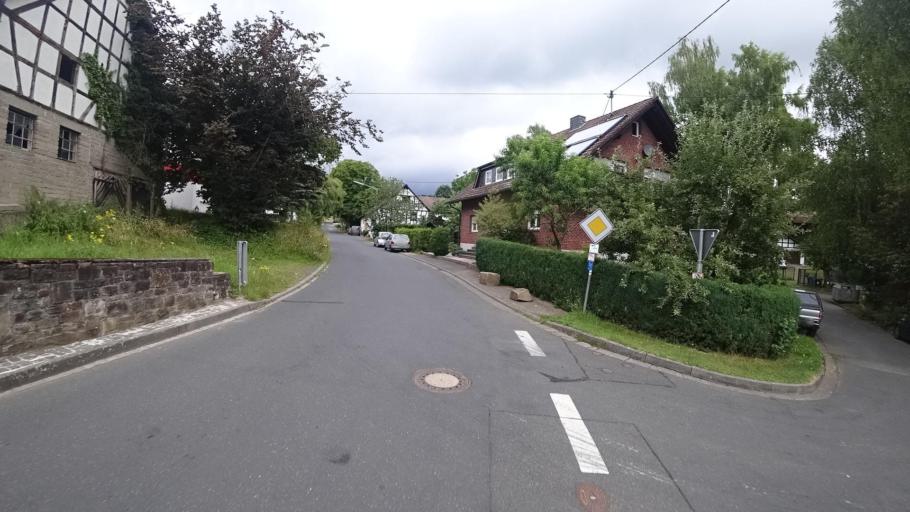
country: DE
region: Rheinland-Pfalz
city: Seifen
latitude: 50.6864
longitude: 7.5092
